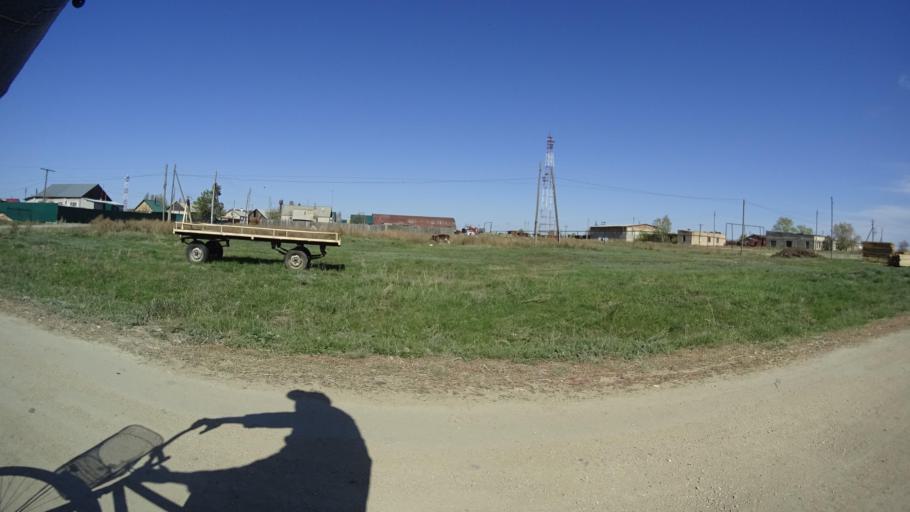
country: RU
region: Chelyabinsk
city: Chesma
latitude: 53.7890
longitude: 61.0381
